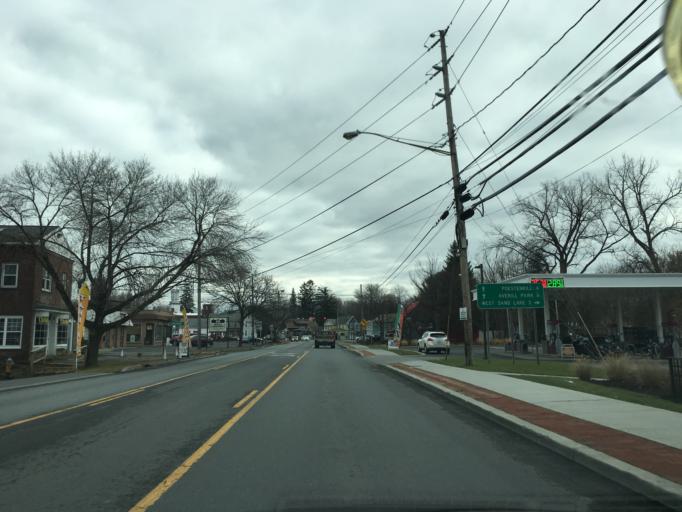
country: US
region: New York
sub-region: Rensselaer County
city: Wynantskill
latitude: 42.6944
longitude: -73.6361
